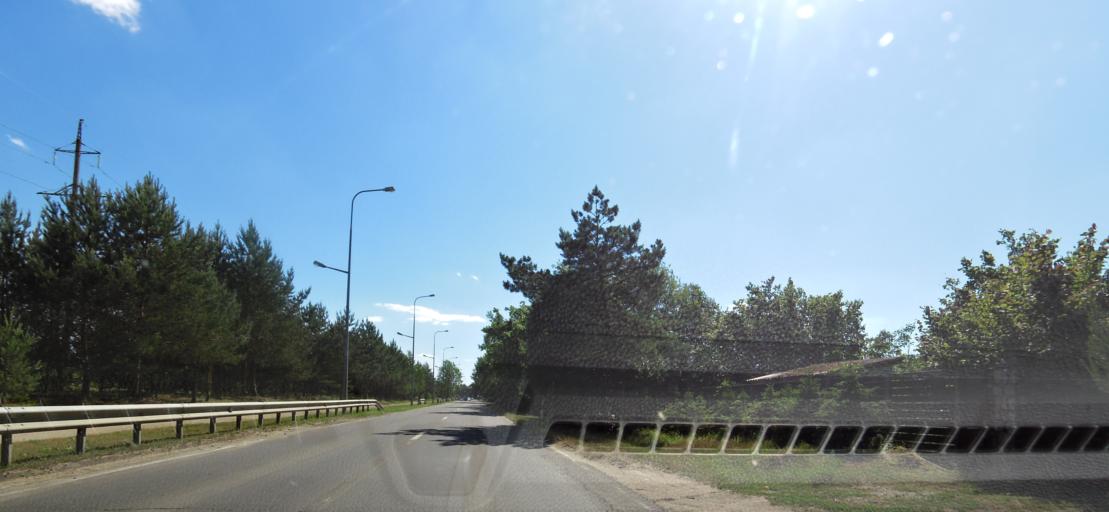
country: LT
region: Vilnius County
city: Rasos
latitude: 54.7835
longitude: 25.3451
